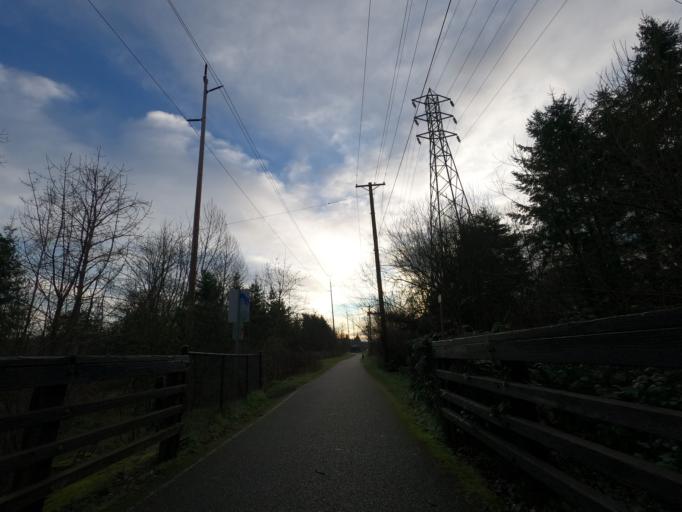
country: US
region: Oregon
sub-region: Clackamas County
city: Milwaukie
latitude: 45.4627
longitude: -122.6203
